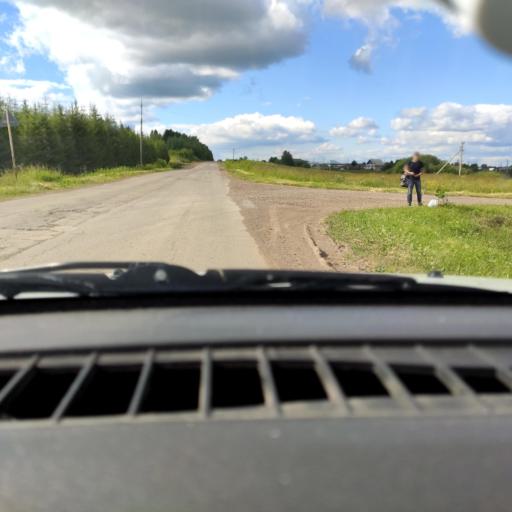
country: RU
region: Perm
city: Uinskoye
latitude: 57.1691
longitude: 56.5649
